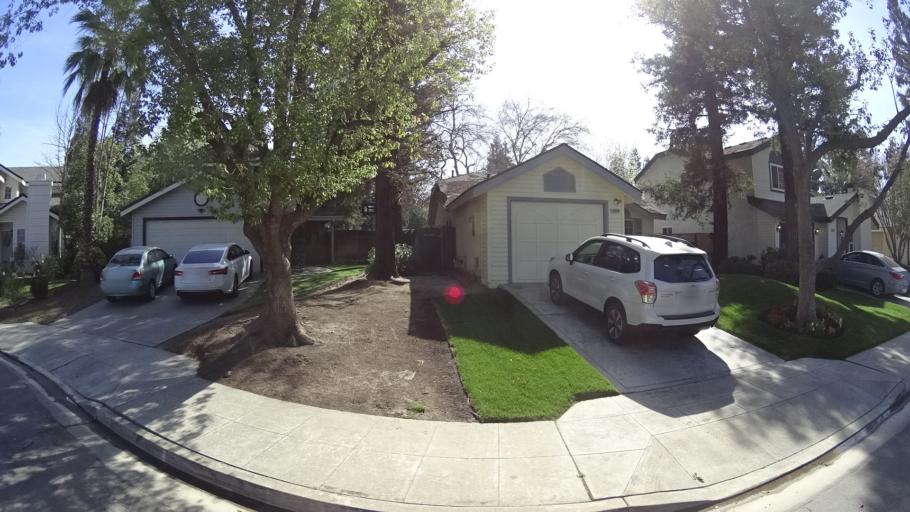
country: US
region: California
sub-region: Fresno County
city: Clovis
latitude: 36.8832
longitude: -119.7677
